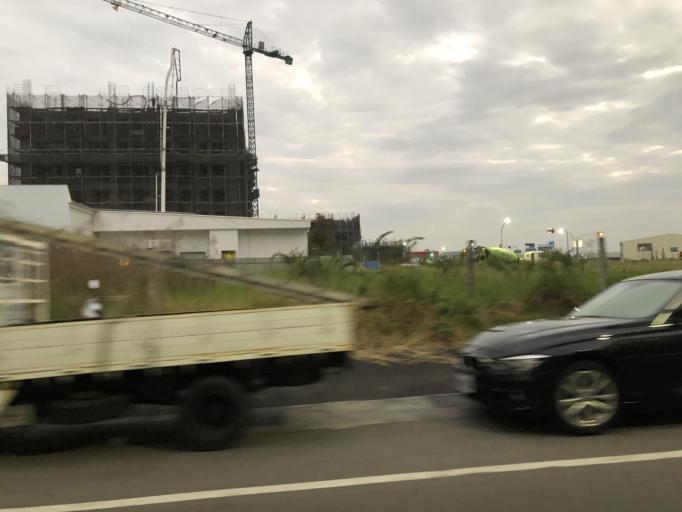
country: TW
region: Taiwan
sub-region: Tainan
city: Tainan
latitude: 23.0156
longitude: 120.2572
